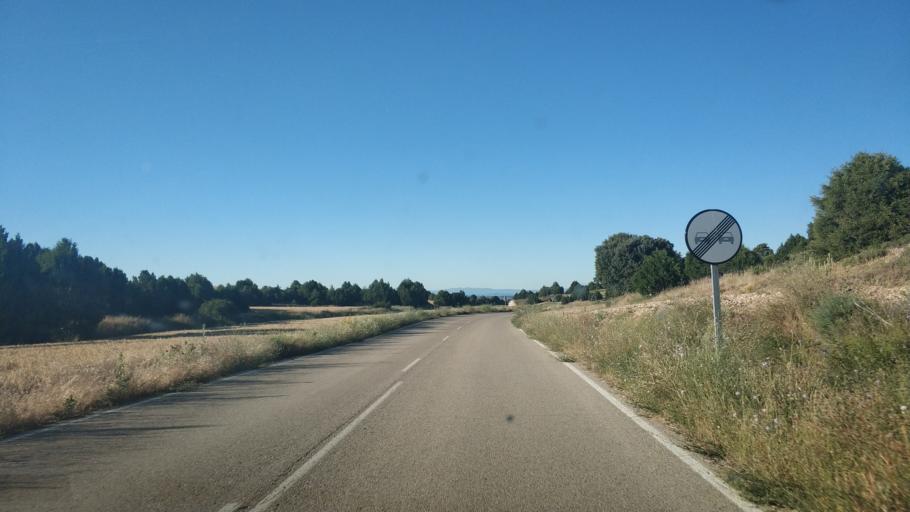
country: ES
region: Castille and Leon
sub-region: Provincia de Soria
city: San Esteban de Gormaz
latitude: 41.4861
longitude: -3.2094
